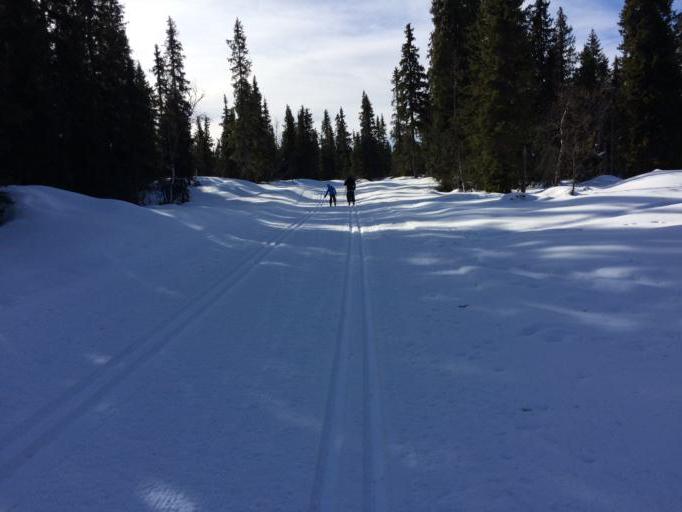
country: NO
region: Oppland
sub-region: Gausdal
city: Segalstad bru
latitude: 61.3269
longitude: 10.0789
